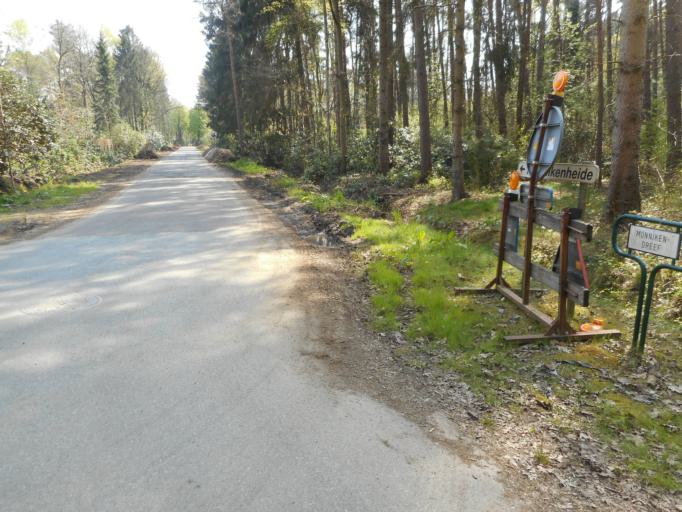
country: BE
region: Flanders
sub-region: Provincie Antwerpen
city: Zoersel
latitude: 51.2623
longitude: 4.6956
